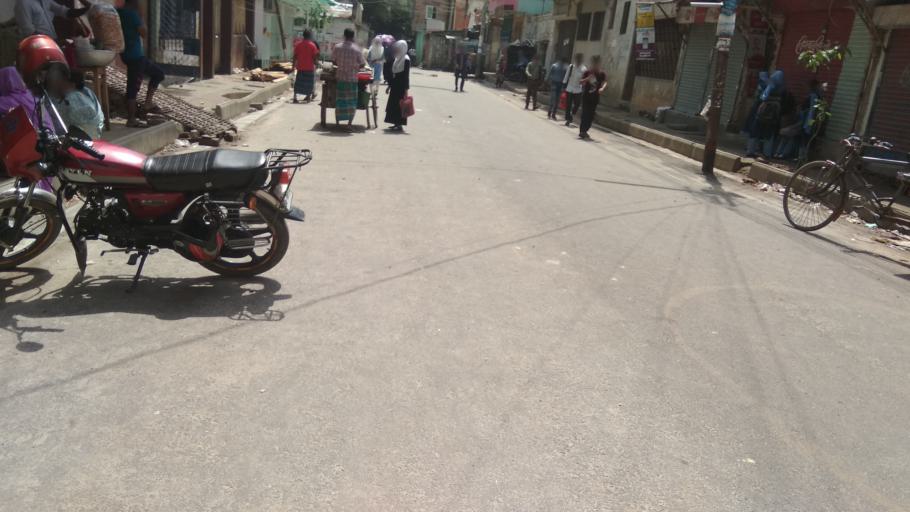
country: BD
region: Dhaka
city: Azimpur
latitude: 23.8122
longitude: 90.3699
